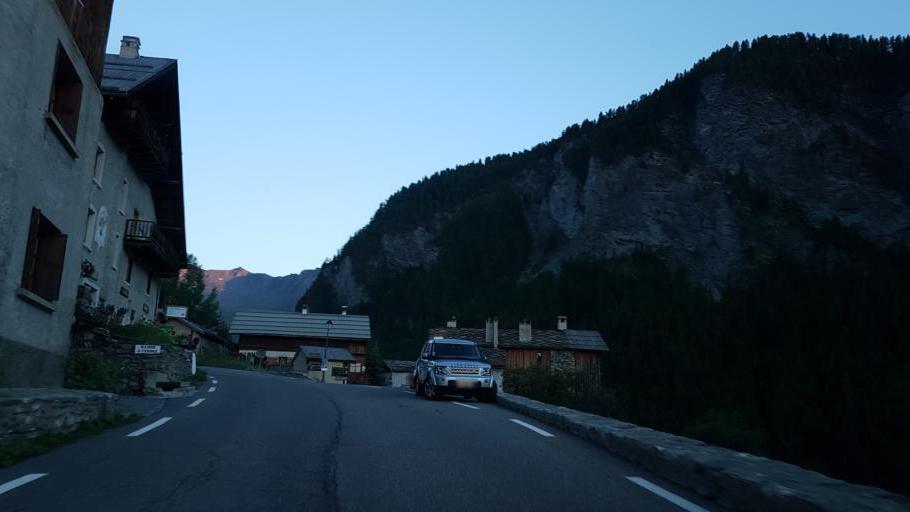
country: IT
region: Piedmont
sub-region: Provincia di Cuneo
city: Pontechianale
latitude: 44.6993
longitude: 6.8617
